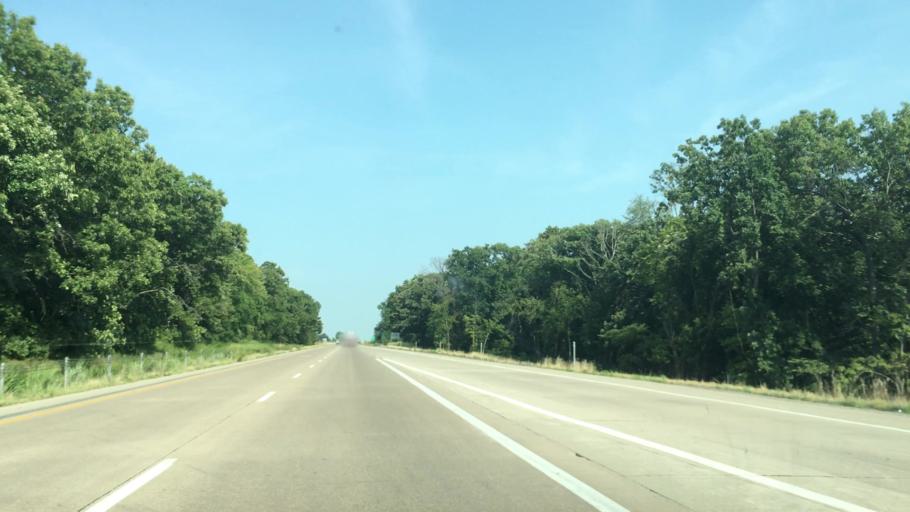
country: US
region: Iowa
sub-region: Muscatine County
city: Wilton
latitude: 41.6389
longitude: -91.0488
